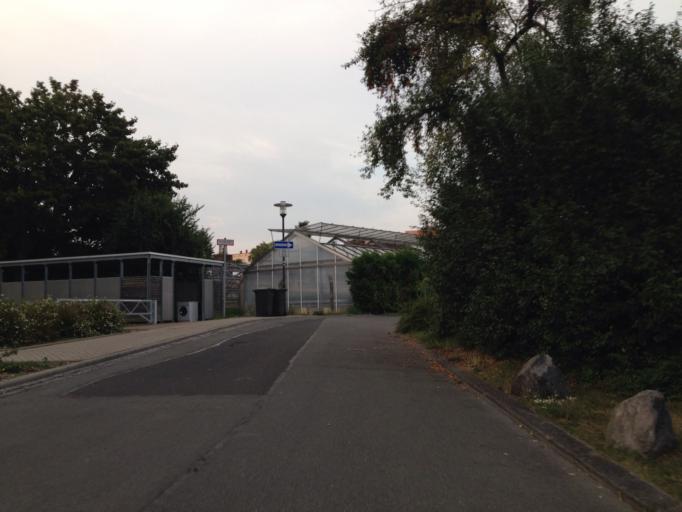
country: DE
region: Hesse
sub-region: Regierungsbezirk Giessen
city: Giessen
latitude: 50.5991
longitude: 8.6823
